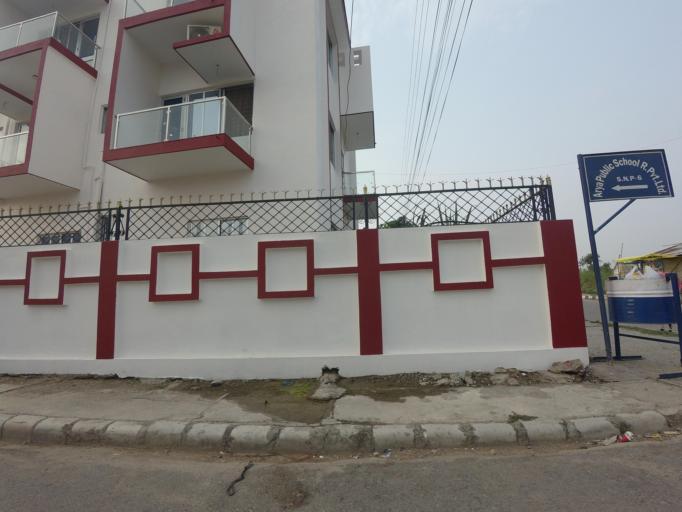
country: NP
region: Western Region
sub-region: Lumbini Zone
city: Bhairahawa
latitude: 27.5024
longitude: 83.4440
